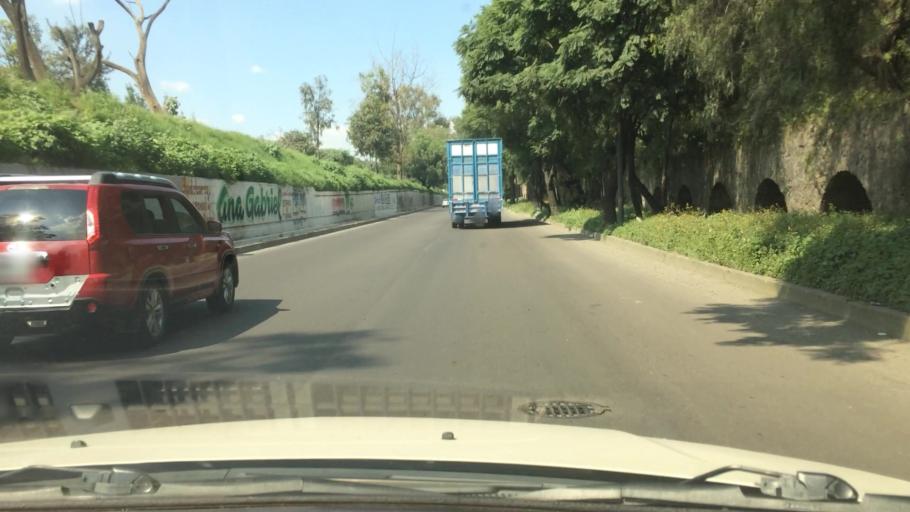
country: MX
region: Mexico
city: Colonia Lindavista
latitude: 19.5213
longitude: -99.1485
